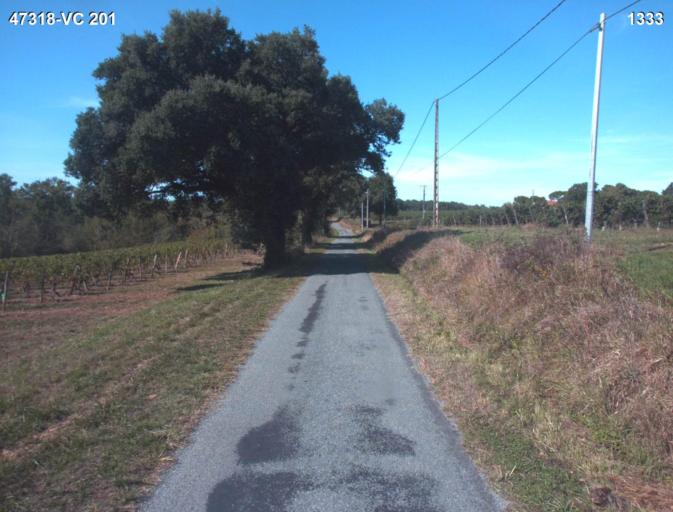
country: FR
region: Aquitaine
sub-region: Departement du Lot-et-Garonne
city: Vianne
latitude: 44.2083
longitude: 0.3137
